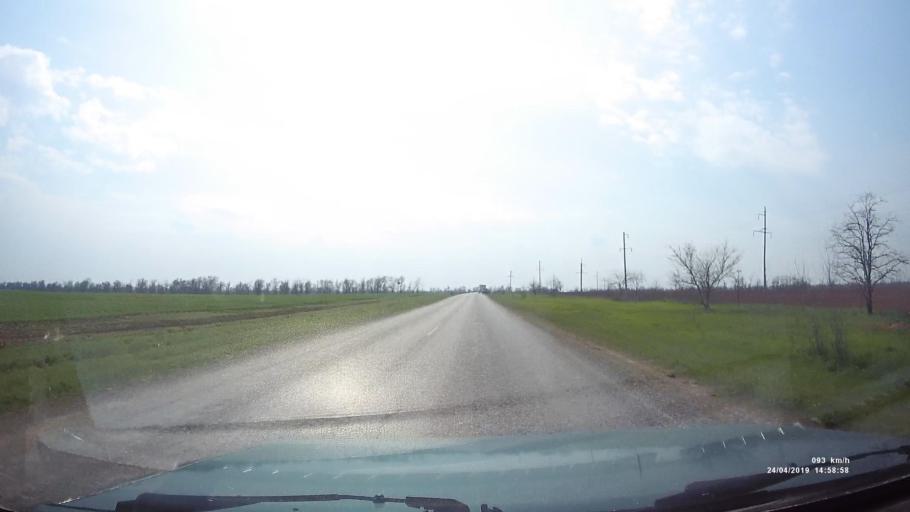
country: RU
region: Rostov
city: Remontnoye
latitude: 46.5680
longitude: 43.5831
